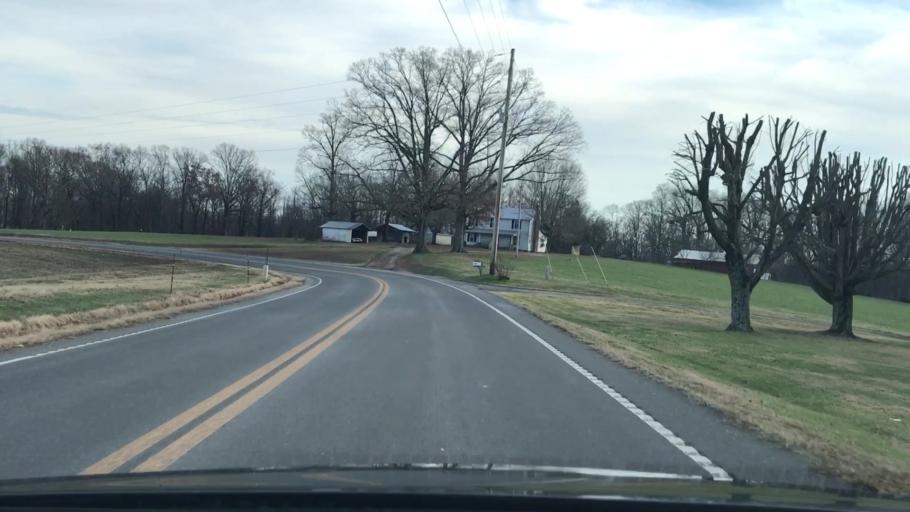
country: US
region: Tennessee
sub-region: Macon County
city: Red Boiling Springs
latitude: 36.5586
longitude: -85.8390
